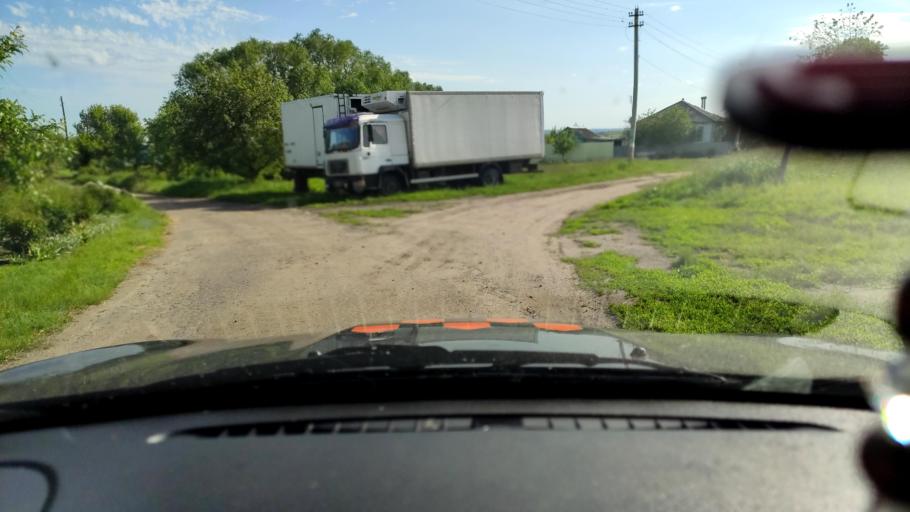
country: RU
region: Voronezj
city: Uryv-Pokrovka
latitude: 51.1207
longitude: 39.1719
